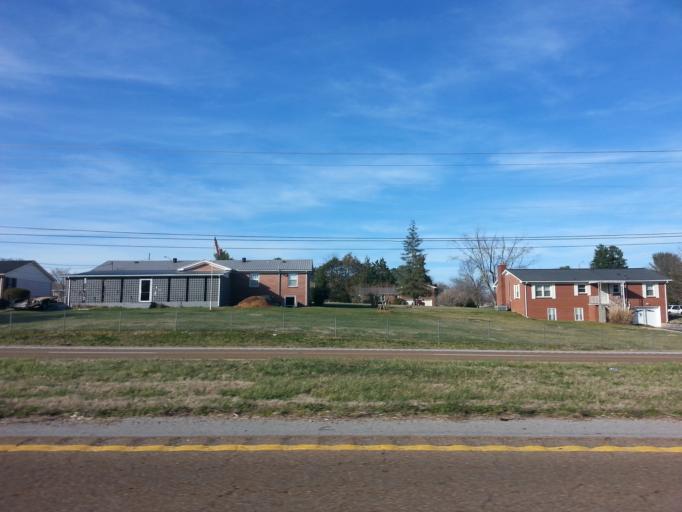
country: US
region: Tennessee
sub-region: Warren County
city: McMinnville
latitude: 35.6999
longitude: -85.7725
